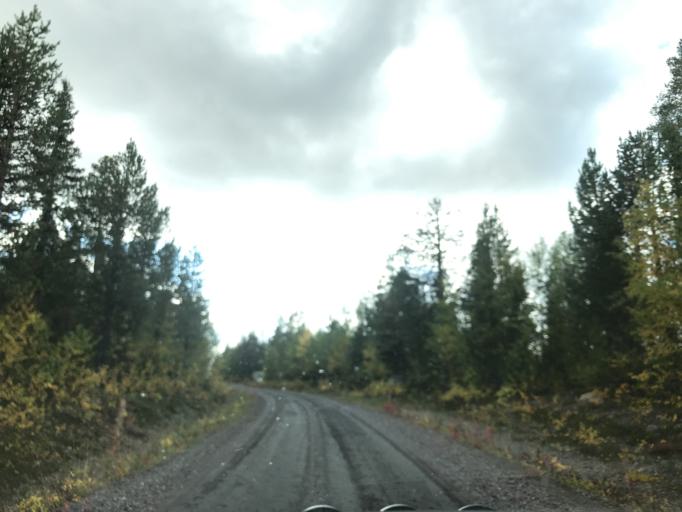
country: SE
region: Norrbotten
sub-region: Gallivare Kommun
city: Malmberget
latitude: 67.5923
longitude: 20.8797
